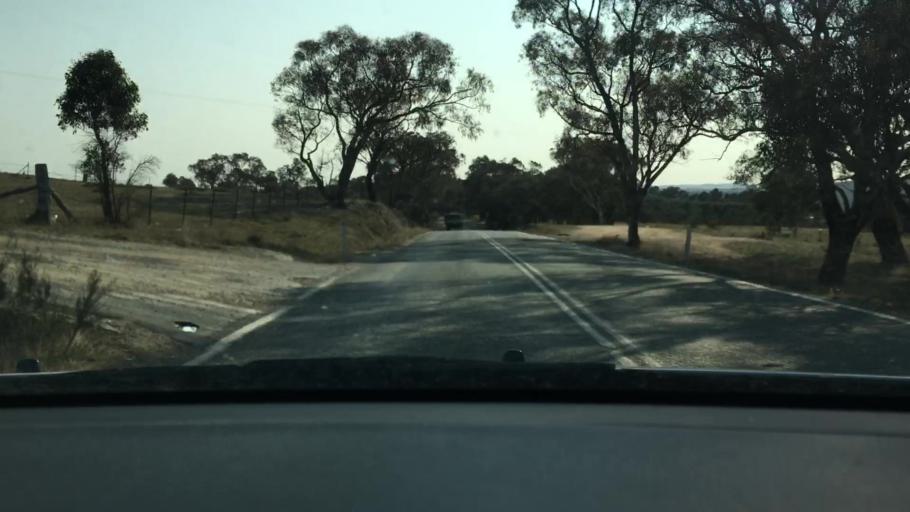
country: AU
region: New South Wales
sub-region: Queanbeyan
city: Queanbeyan
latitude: -35.4075
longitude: 149.2274
